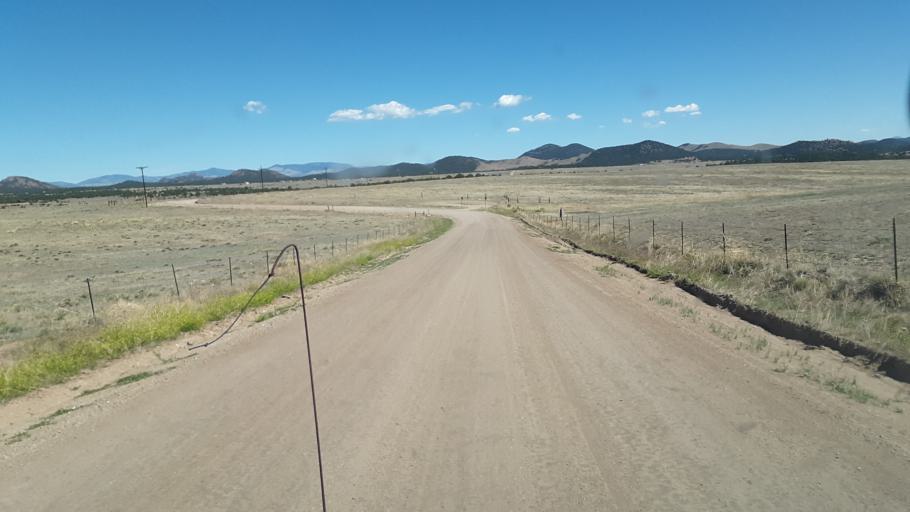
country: US
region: Colorado
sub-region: Custer County
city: Westcliffe
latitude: 38.2609
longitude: -105.4999
